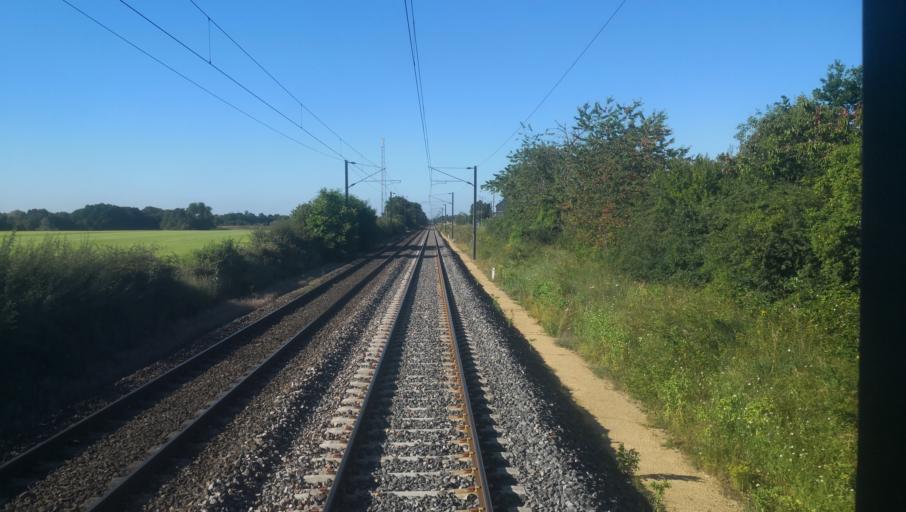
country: FR
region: Bourgogne
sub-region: Departement de la Nievre
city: Cosne-Cours-sur-Loire
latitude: 47.3766
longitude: 2.9029
